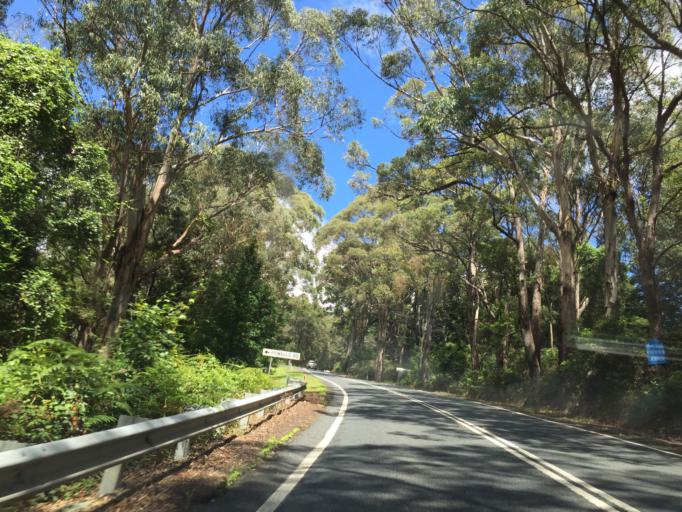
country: AU
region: New South Wales
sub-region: Blue Mountains Municipality
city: Lawson
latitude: -33.5175
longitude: 150.4667
